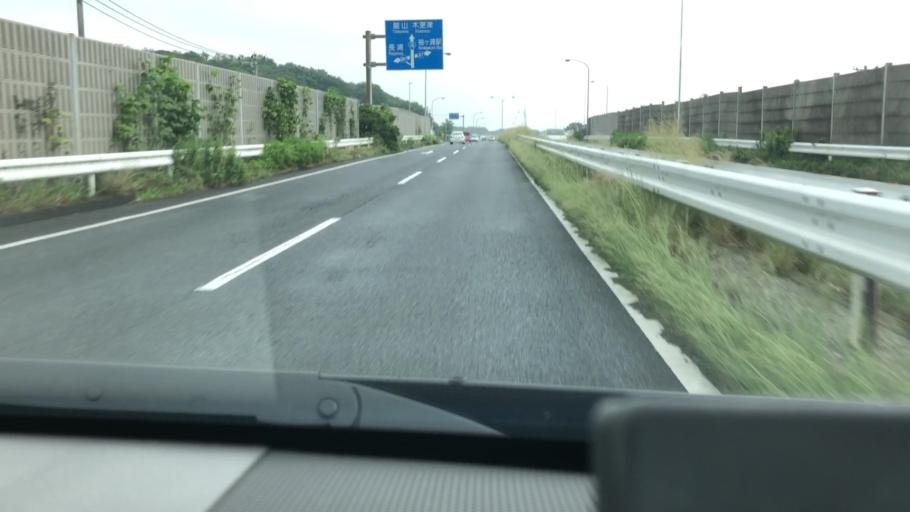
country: JP
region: Chiba
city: Kisarazu
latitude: 35.4399
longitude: 139.9713
